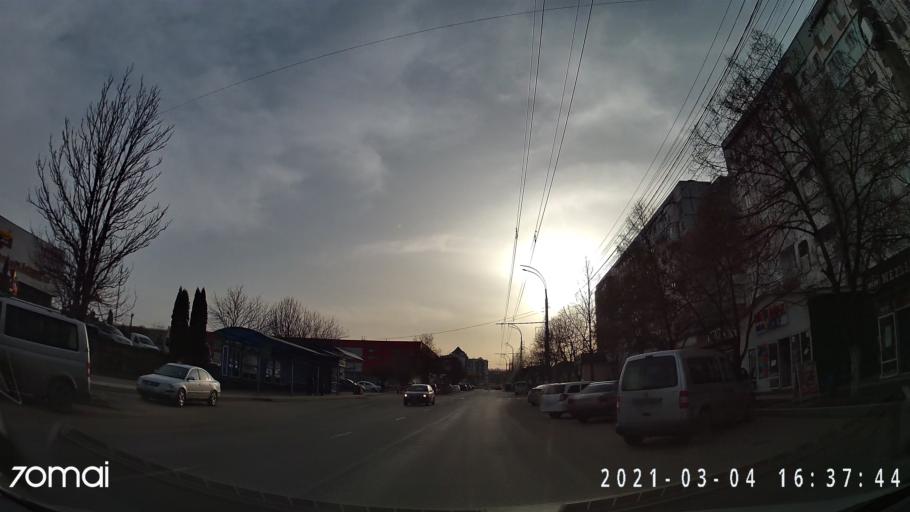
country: MD
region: Balti
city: Balti
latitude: 47.7830
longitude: 27.8925
